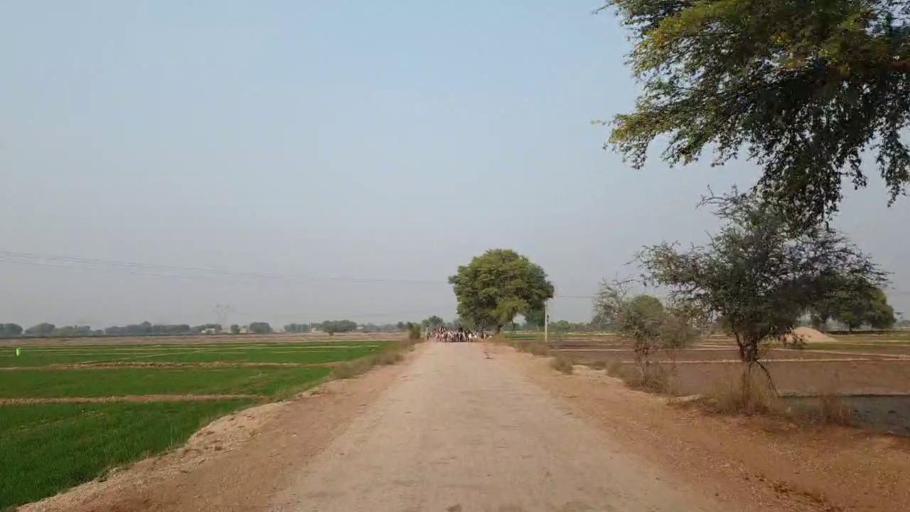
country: PK
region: Sindh
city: Bhan
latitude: 26.4977
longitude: 67.7504
